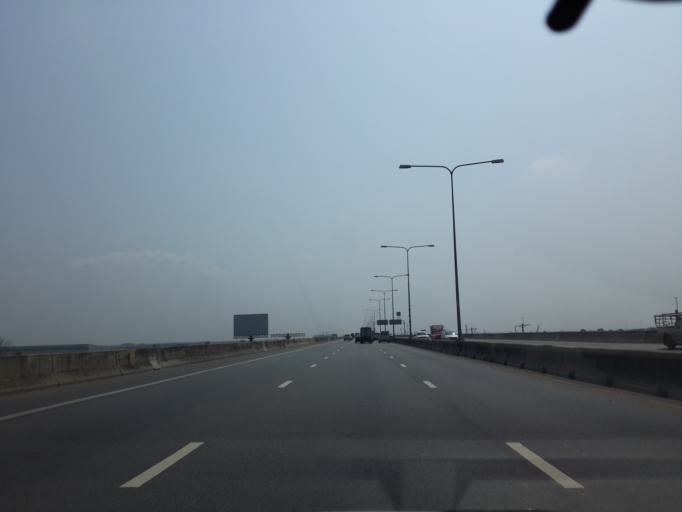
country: TH
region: Samut Prakan
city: Bang Bo
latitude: 13.5812
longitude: 100.8692
